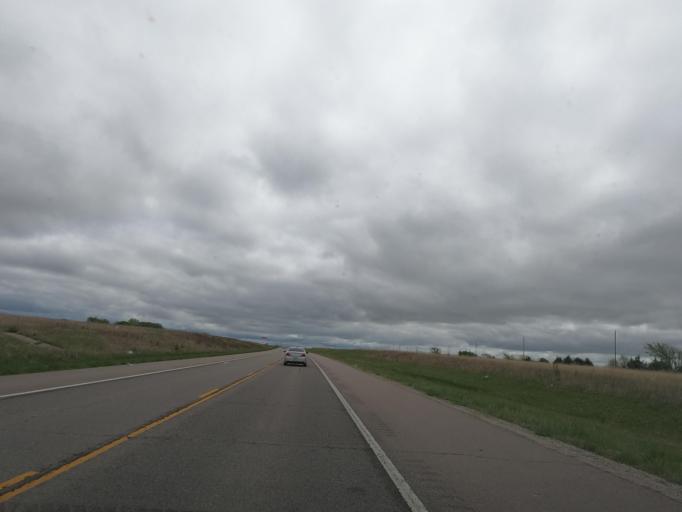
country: US
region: Kansas
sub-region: Elk County
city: Howard
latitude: 37.6359
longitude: -96.2608
